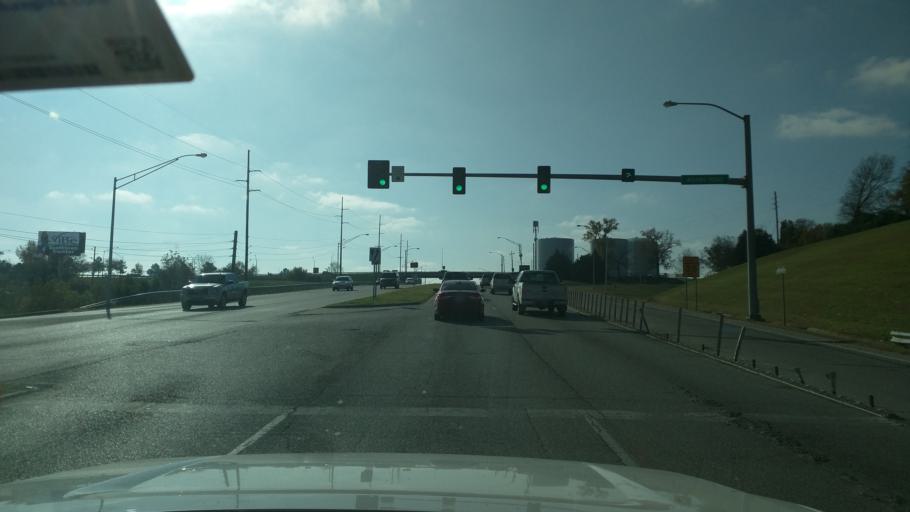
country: US
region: Oklahoma
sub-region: Washington County
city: Bartlesville
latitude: 36.7457
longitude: -95.9355
